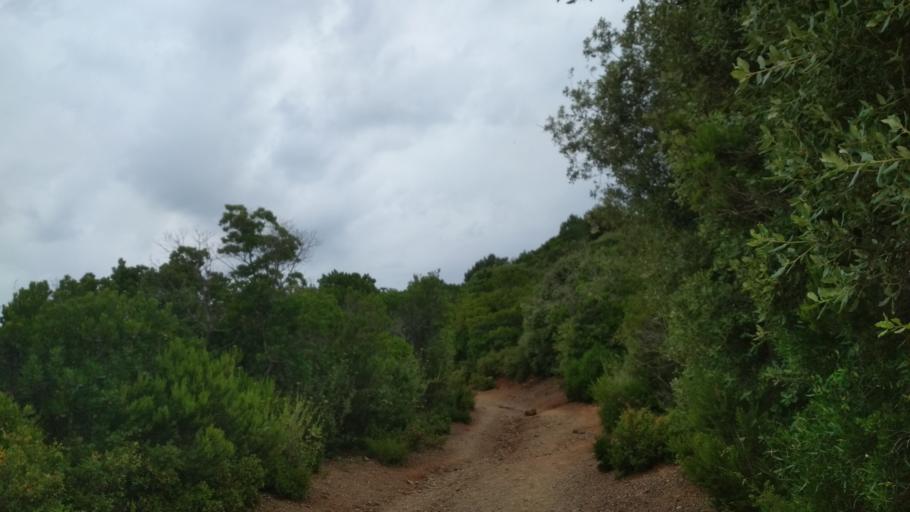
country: ES
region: Catalonia
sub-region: Provincia de Barcelona
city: Horta-Guinardo
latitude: 41.4429
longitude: 2.1393
